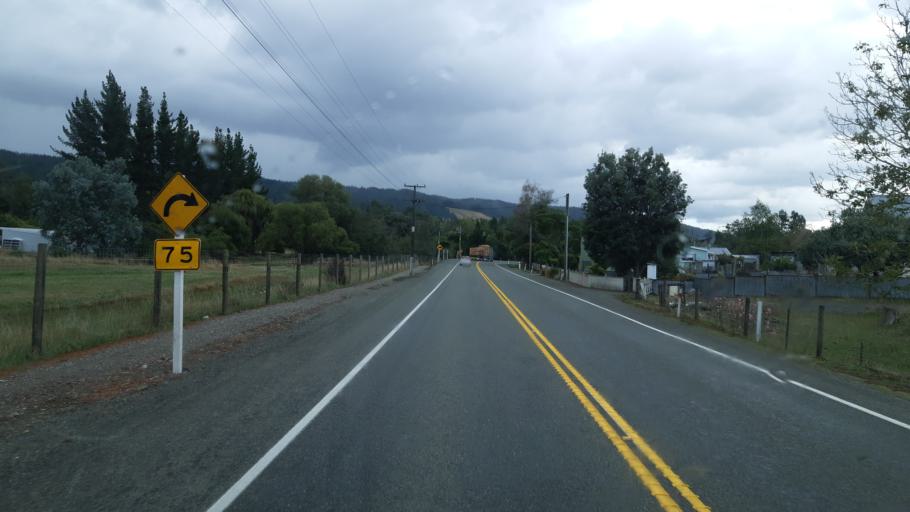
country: NZ
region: Tasman
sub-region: Tasman District
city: Wakefield
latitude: -41.4526
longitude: 172.9574
